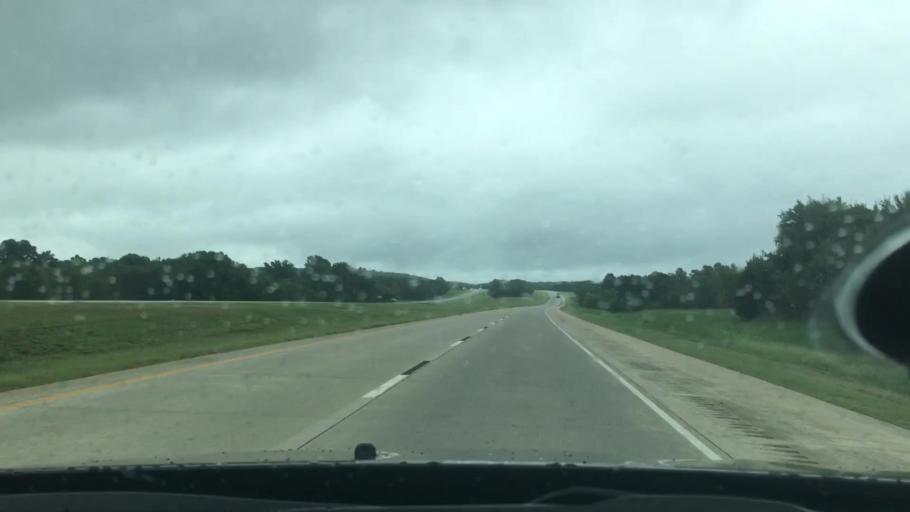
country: US
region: Oklahoma
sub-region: Okmulgee County
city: Henryetta
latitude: 35.4319
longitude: -95.8803
